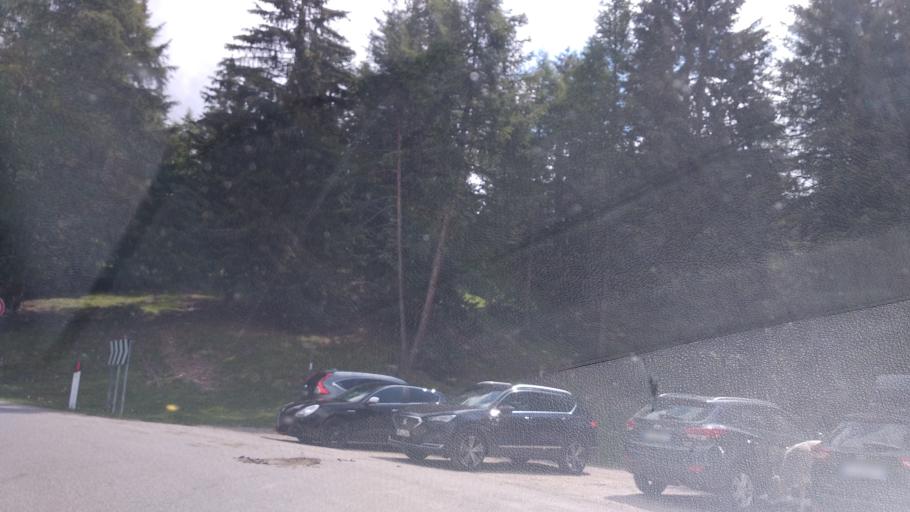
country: IT
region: Trentino-Alto Adige
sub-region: Bolzano
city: Avelengo
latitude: 46.6562
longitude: 11.2293
